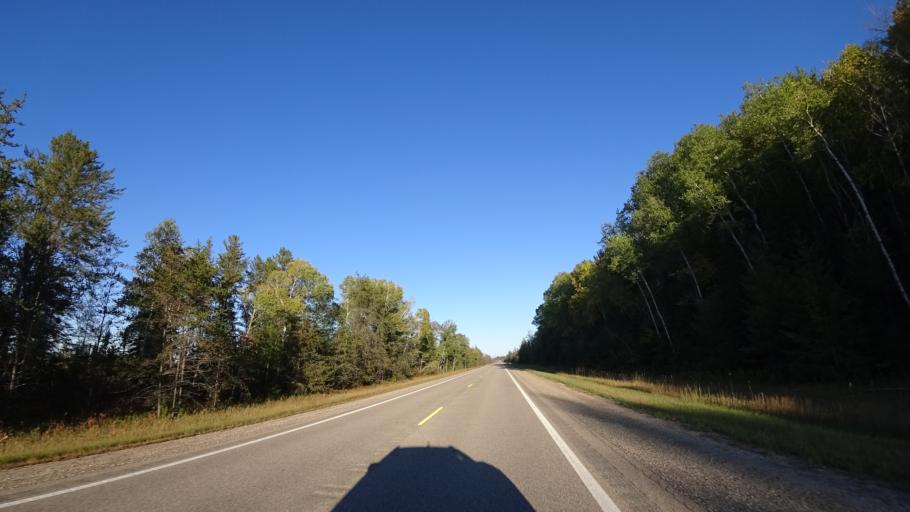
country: US
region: Michigan
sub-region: Luce County
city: Newberry
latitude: 46.3410
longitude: -85.9137
